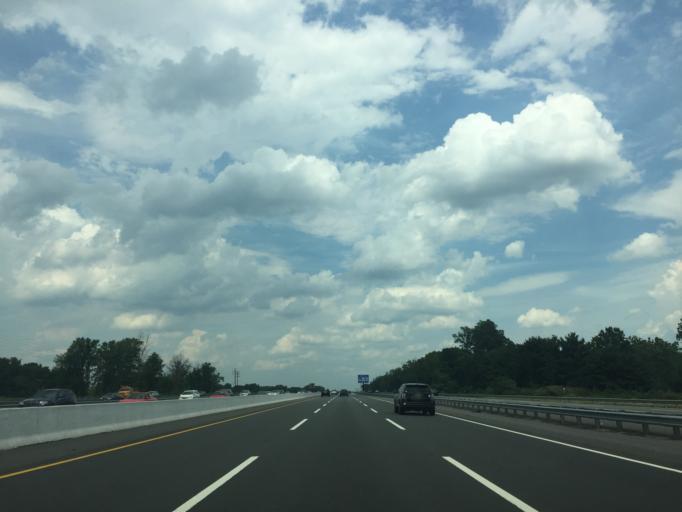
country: US
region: New Jersey
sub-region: Mercer County
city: Groveville
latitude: 40.1455
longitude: -74.6735
